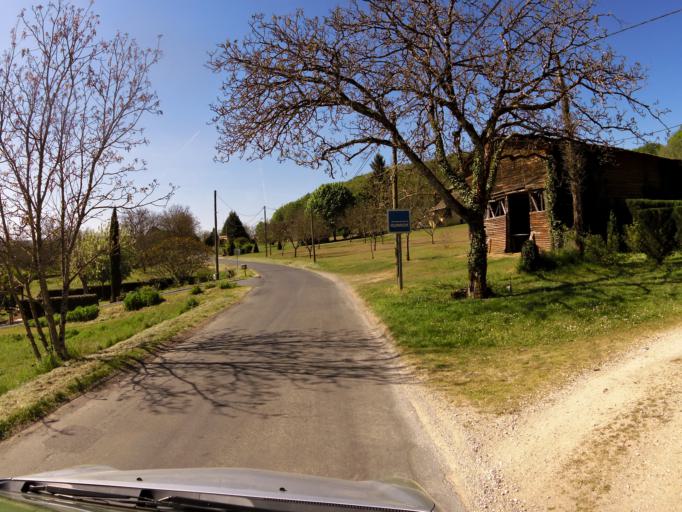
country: FR
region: Aquitaine
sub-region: Departement de la Dordogne
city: Carsac-Aillac
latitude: 44.8436
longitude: 1.2280
